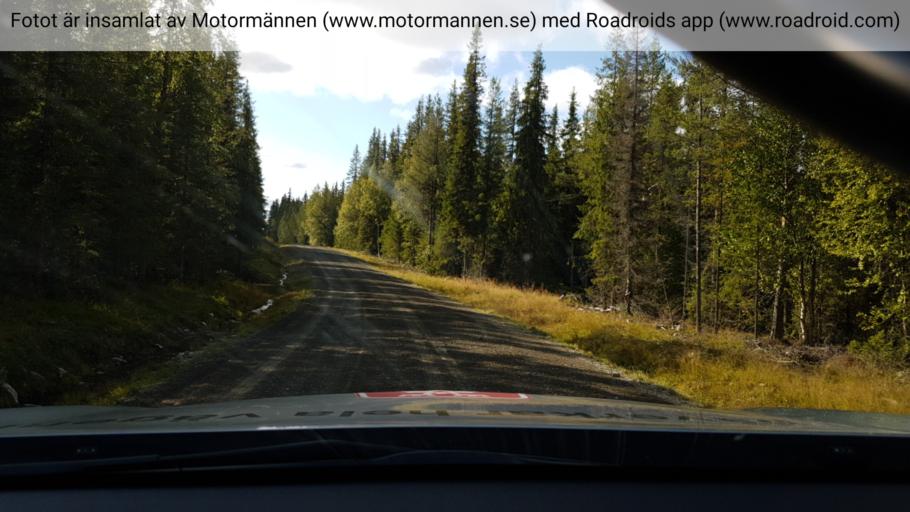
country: SE
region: Vaesterbotten
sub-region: Mala Kommun
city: Mala
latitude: 65.4863
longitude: 18.2288
